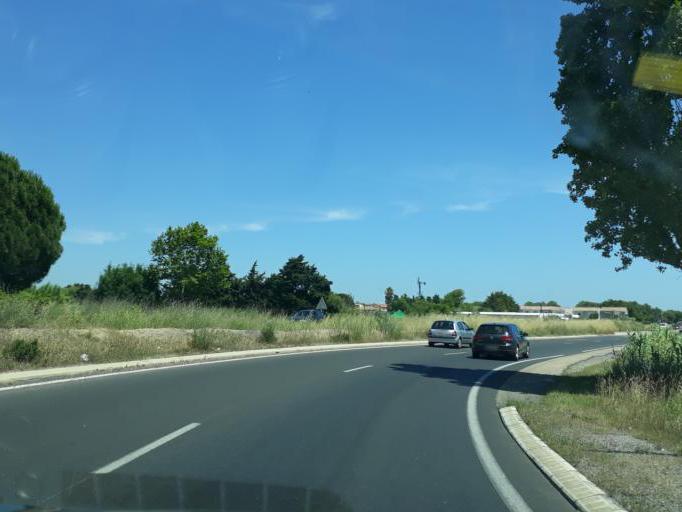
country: FR
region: Languedoc-Roussillon
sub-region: Departement de l'Herault
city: Cers
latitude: 43.3203
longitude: 3.2942
